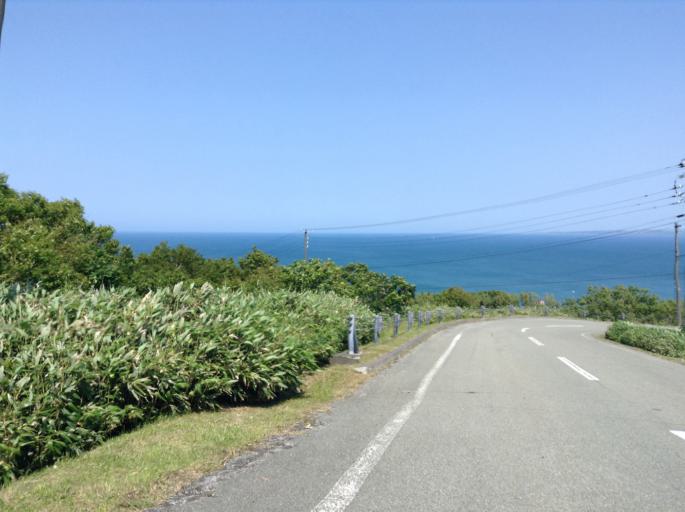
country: JP
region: Hokkaido
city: Wakkanai
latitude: 45.4187
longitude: 141.6684
